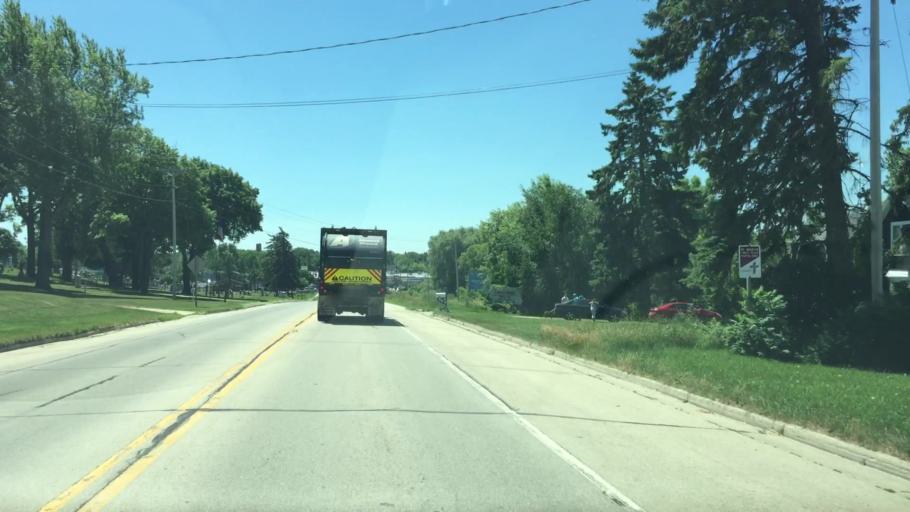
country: US
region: Wisconsin
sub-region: Calumet County
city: Chilton
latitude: 44.0414
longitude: -88.1630
